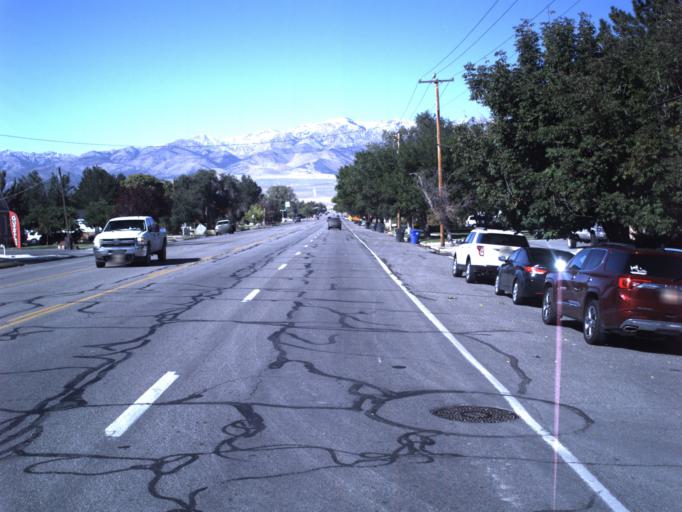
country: US
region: Utah
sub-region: Tooele County
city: Grantsville
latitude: 40.5999
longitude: -112.4580
